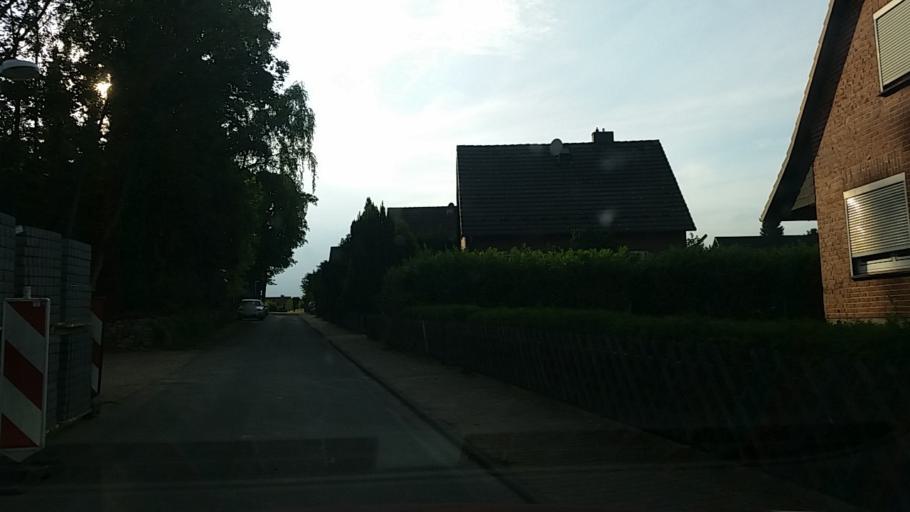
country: DE
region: Lower Saxony
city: Adendorf
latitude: 53.2586
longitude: 10.4692
